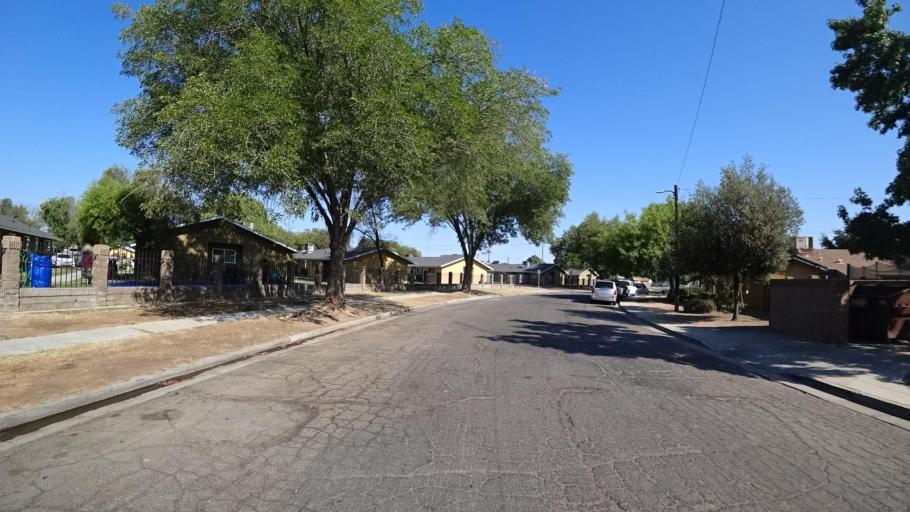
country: US
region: California
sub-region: Fresno County
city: West Park
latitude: 36.7203
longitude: -119.8231
